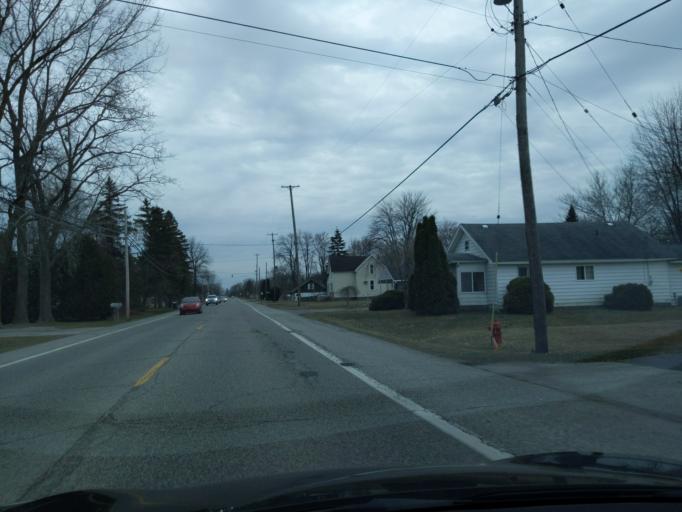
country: US
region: Michigan
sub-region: Bay County
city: Bay City
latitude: 43.6478
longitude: -83.9130
